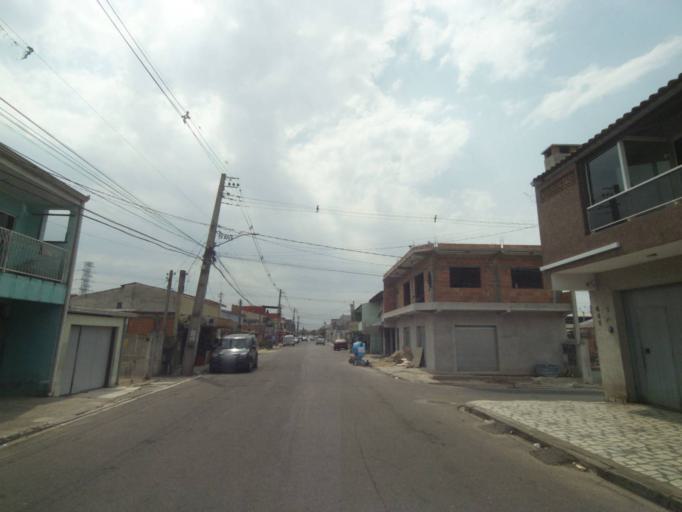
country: BR
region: Parana
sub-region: Pinhais
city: Pinhais
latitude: -25.4870
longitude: -49.1997
